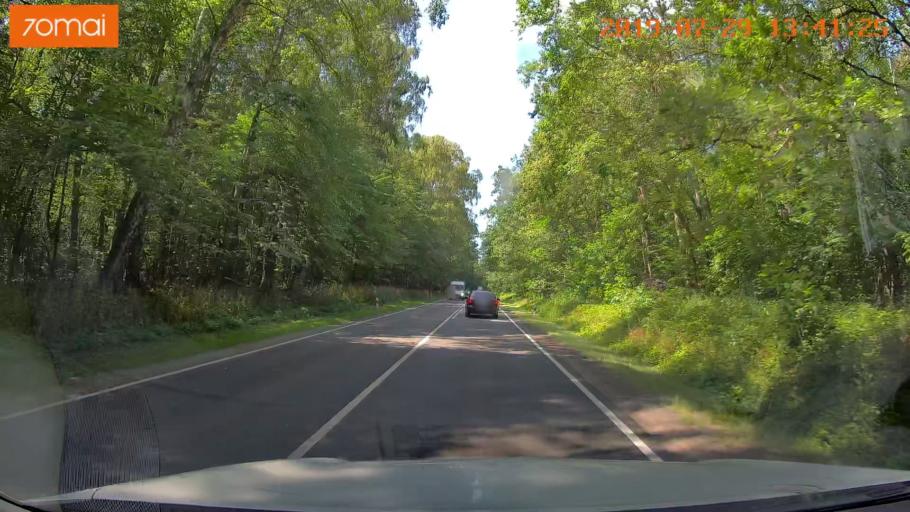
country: RU
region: Kaliningrad
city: Svetlyy
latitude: 54.7353
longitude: 20.1269
